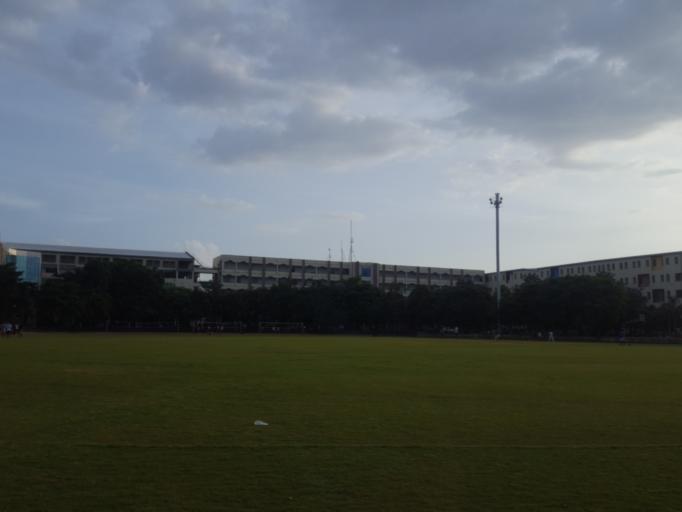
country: IN
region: Telangana
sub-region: Rangareddi
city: Quthbullapur
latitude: 17.5958
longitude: 78.4422
